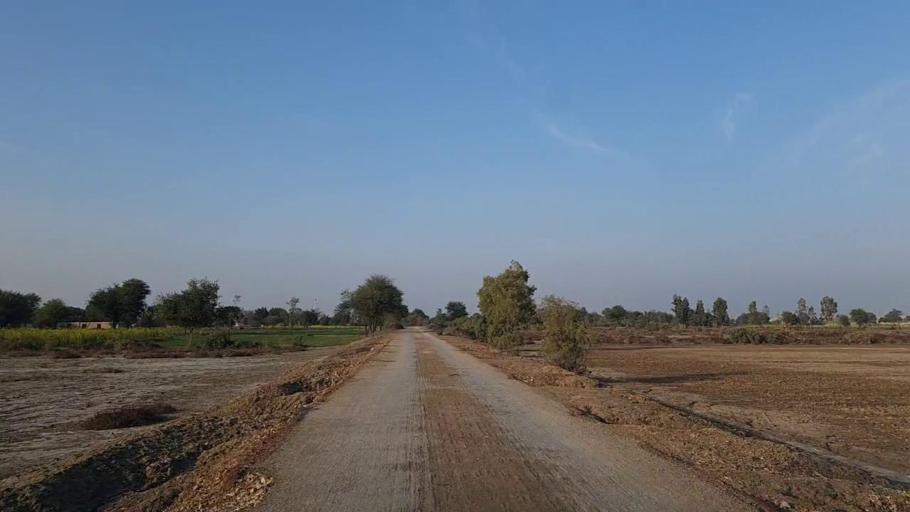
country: PK
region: Sindh
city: Jam Sahib
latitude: 26.3911
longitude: 68.5431
